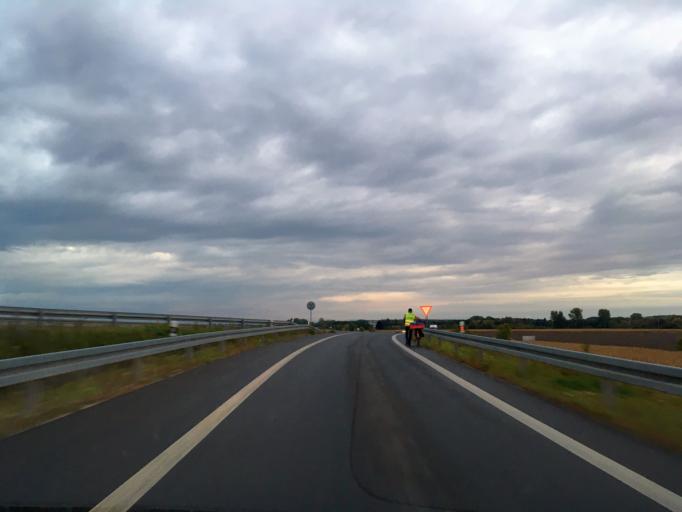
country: SK
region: Trnavsky
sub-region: Okres Galanta
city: Galanta
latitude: 48.1887
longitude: 17.6985
